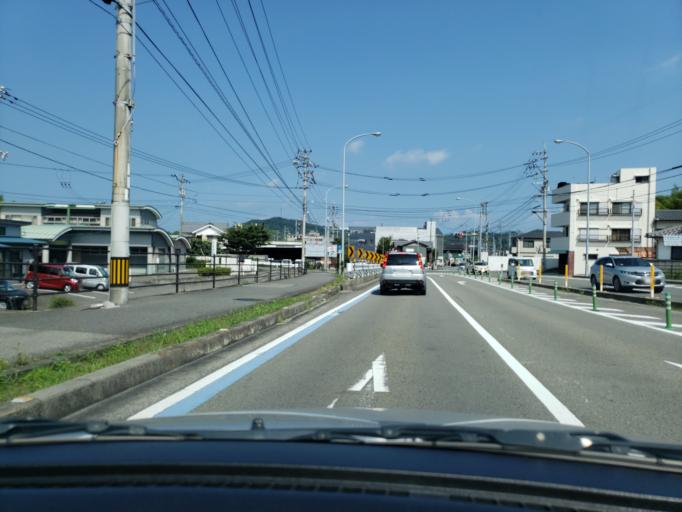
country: JP
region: Ehime
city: Hojo
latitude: 34.0946
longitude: 132.9758
